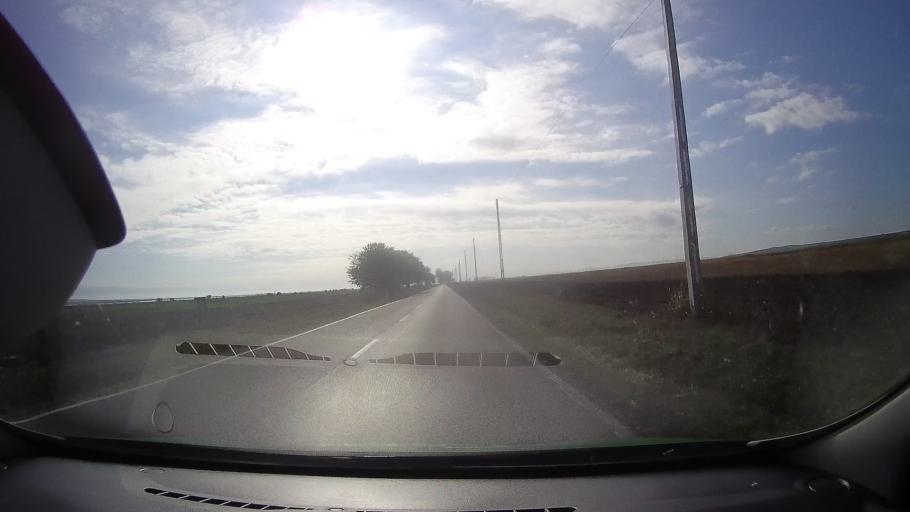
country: RO
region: Tulcea
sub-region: Comuna Valea Nucarilor
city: Agighiol
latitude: 45.0191
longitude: 28.8829
